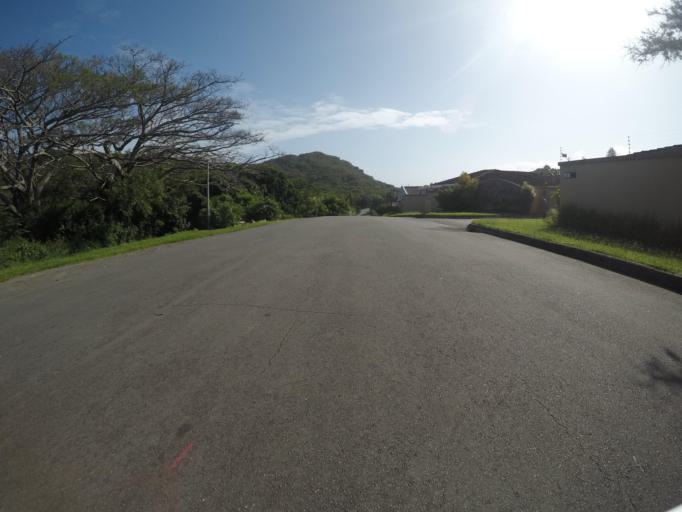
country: ZA
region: Eastern Cape
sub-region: Buffalo City Metropolitan Municipality
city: East London
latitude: -32.9740
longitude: 27.9606
